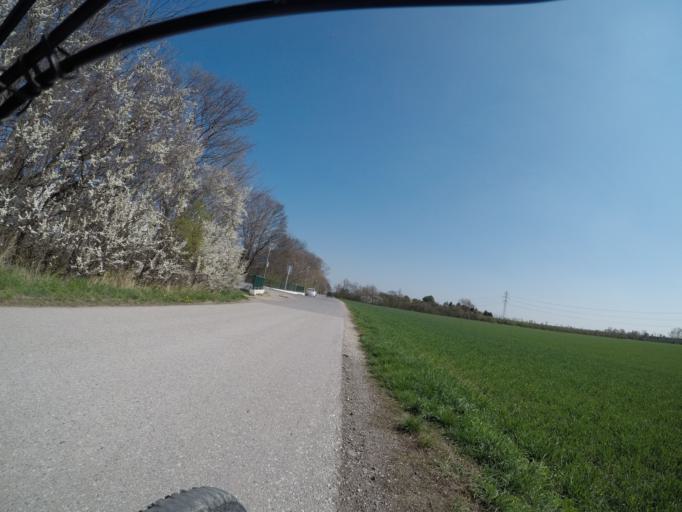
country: AT
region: Lower Austria
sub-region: Politischer Bezirk Modling
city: Biedermannsdorf
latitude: 48.0810
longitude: 16.3418
